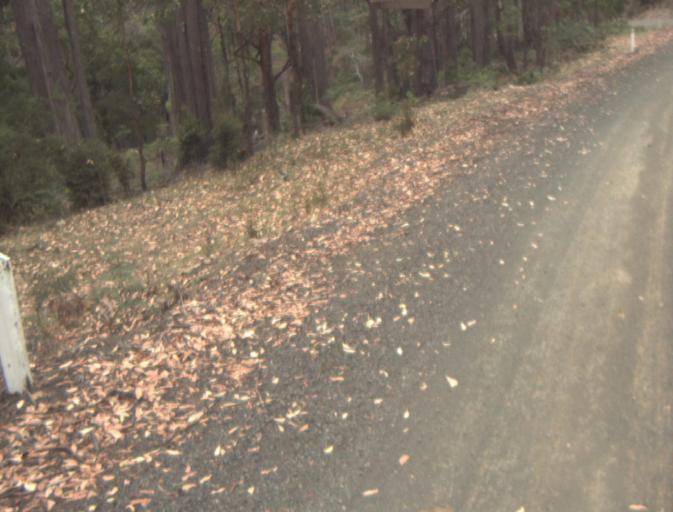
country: AU
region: Tasmania
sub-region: Northern Midlands
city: Evandale
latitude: -41.4950
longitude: 147.5501
